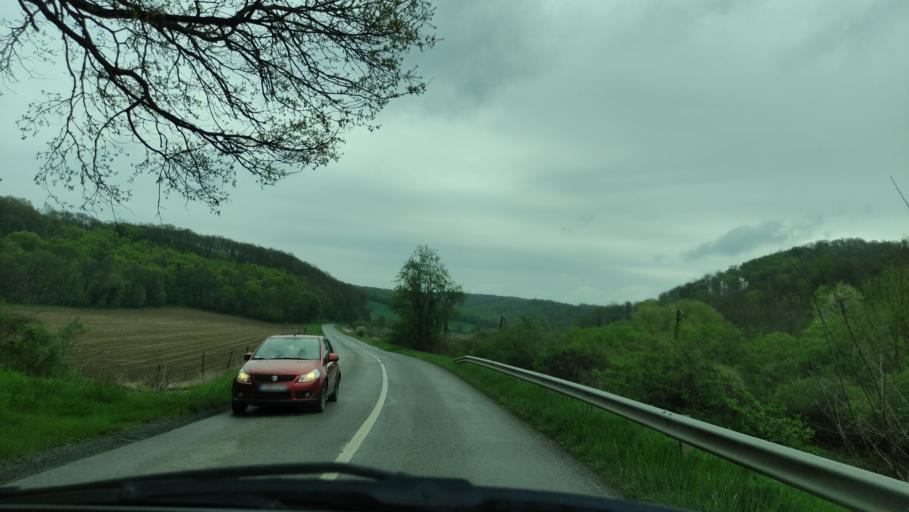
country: HU
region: Baranya
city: Komlo
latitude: 46.2239
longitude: 18.2234
